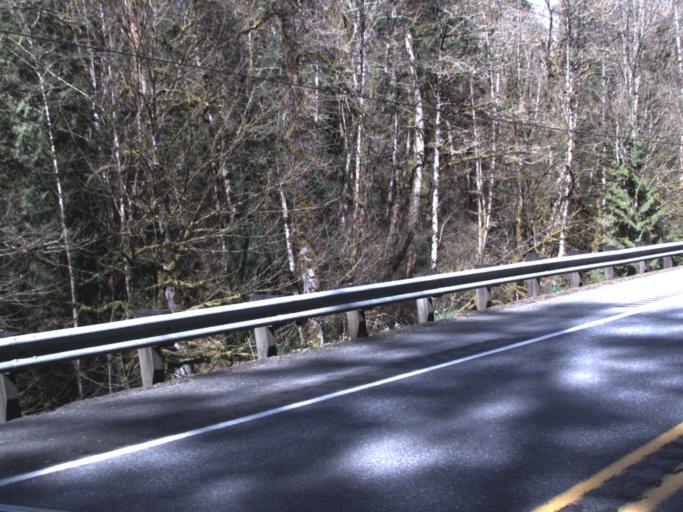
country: US
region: Washington
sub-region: King County
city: Black Diamond
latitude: 47.2739
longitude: -121.9929
